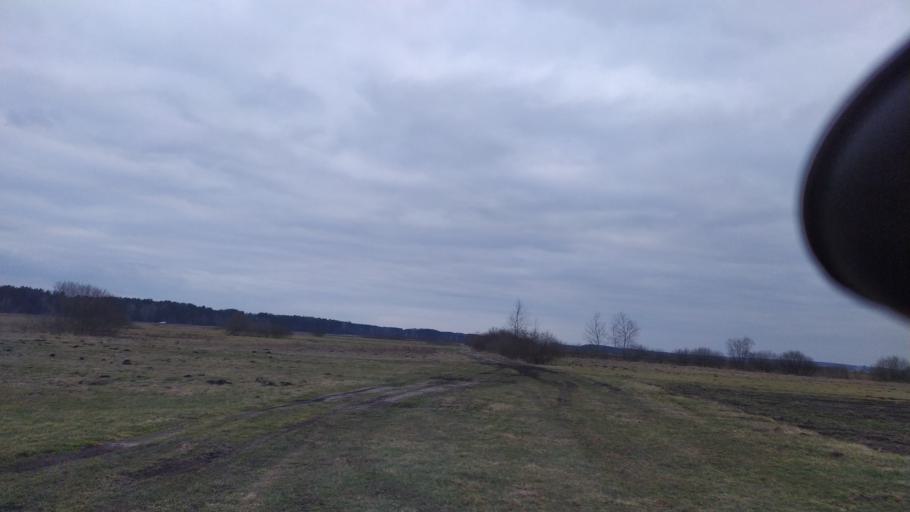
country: PL
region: Lublin Voivodeship
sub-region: Powiat lubartowski
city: Abramow
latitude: 51.4309
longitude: 22.3212
